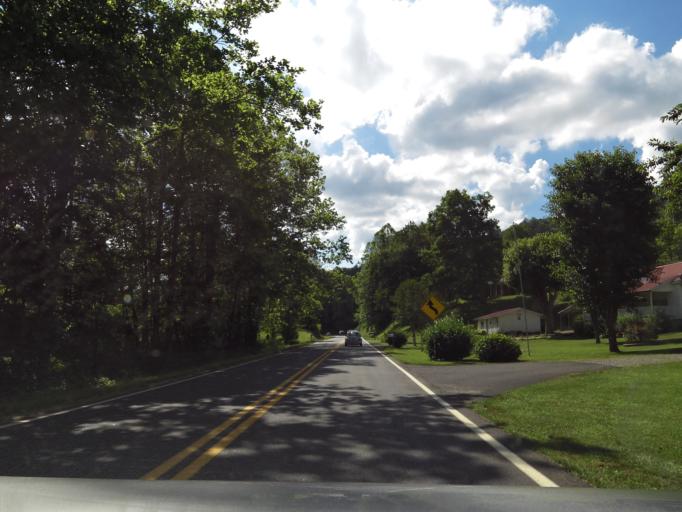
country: US
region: Georgia
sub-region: Towns County
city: Hiawassee
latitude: 34.8335
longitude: -83.7347
